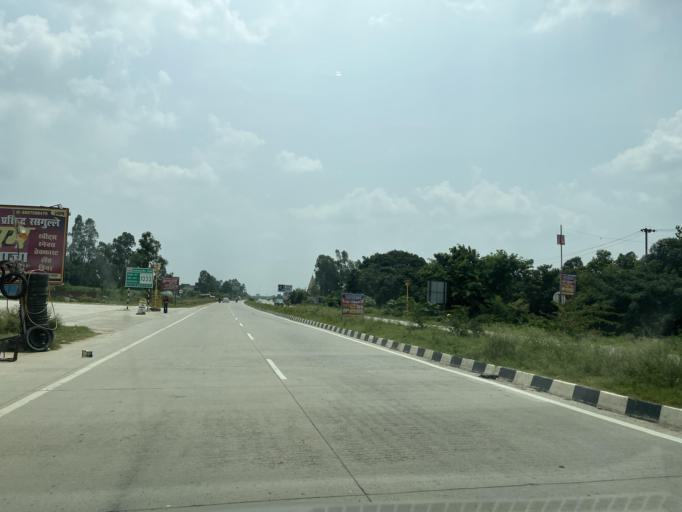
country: IN
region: Uttar Pradesh
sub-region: Bijnor
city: Nagina
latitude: 29.4194
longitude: 78.4453
